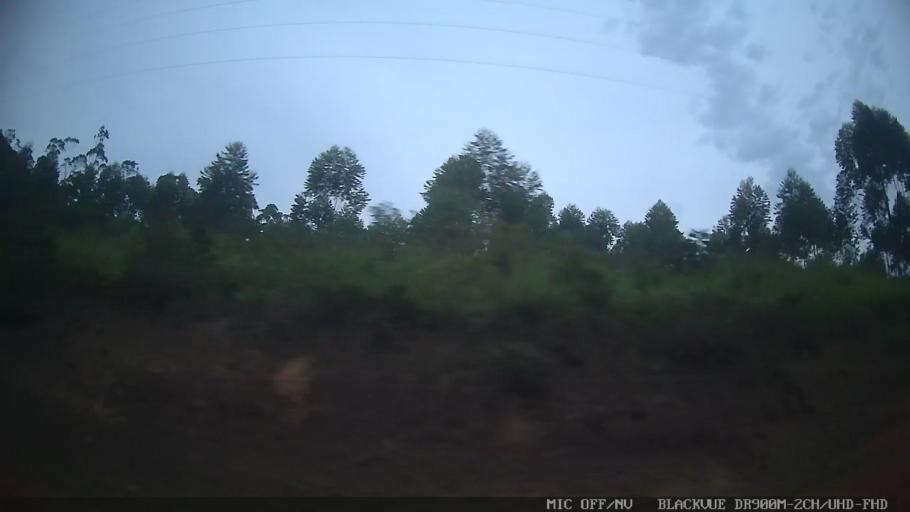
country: BR
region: Sao Paulo
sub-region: Rio Grande Da Serra
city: Rio Grande da Serra
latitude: -23.7056
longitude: -46.3088
